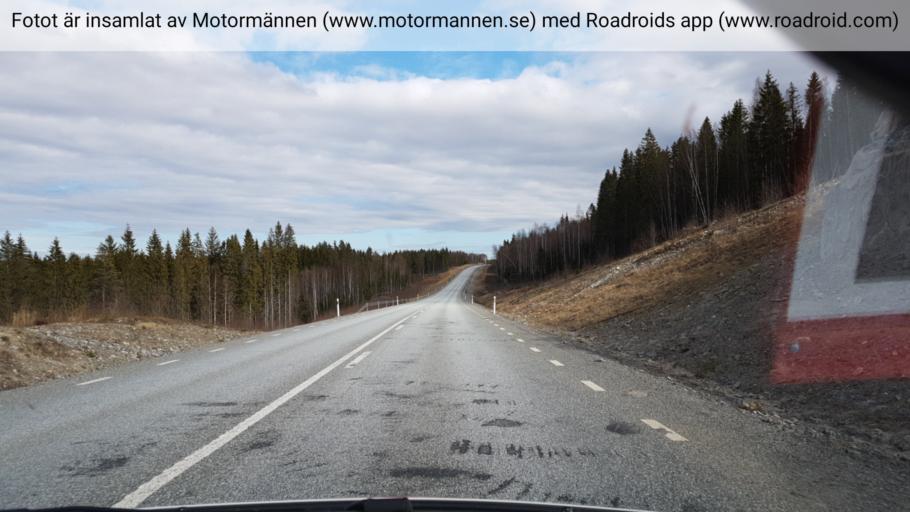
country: SE
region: Vaesternorrland
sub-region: Kramfors Kommun
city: Bollstabruk
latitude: 63.0638
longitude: 17.5931
